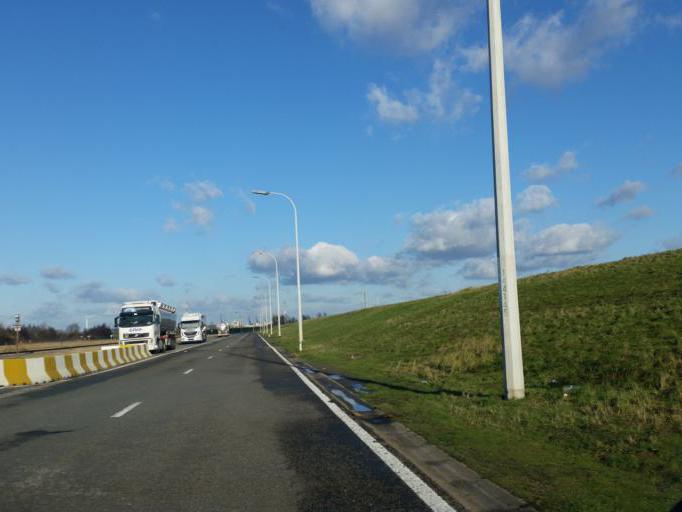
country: BE
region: Flanders
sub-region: Provincie Antwerpen
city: Zwijndrecht
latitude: 51.2792
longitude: 4.3084
